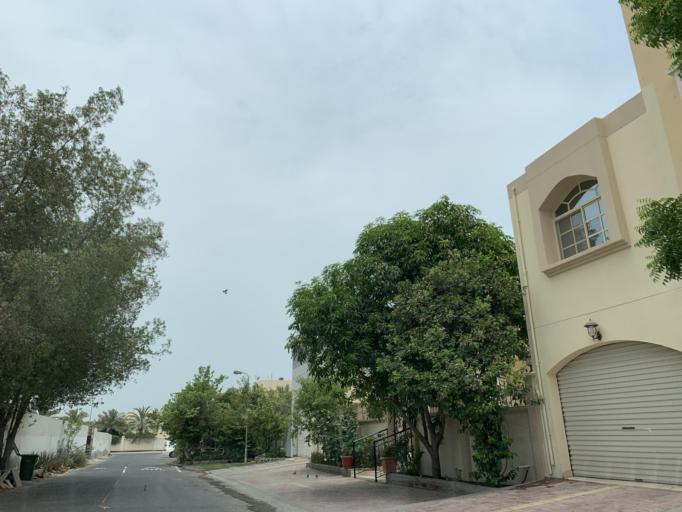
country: BH
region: Northern
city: Madinat `Isa
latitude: 26.1873
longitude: 50.4724
